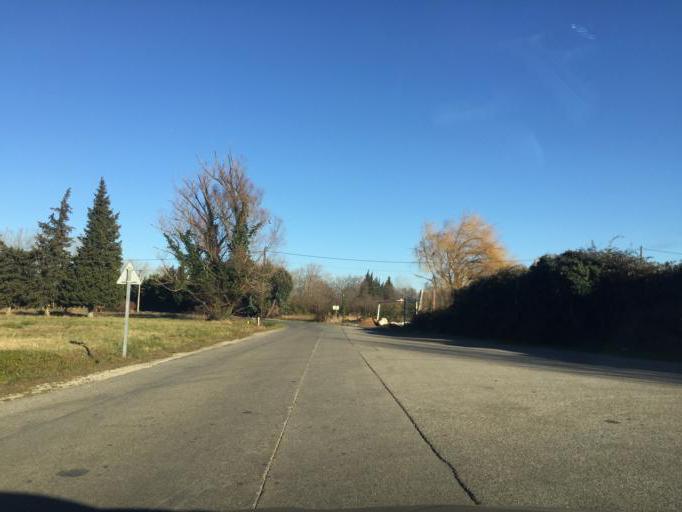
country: FR
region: Provence-Alpes-Cote d'Azur
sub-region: Departement du Vaucluse
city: Vedene
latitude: 43.9903
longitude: 4.9014
